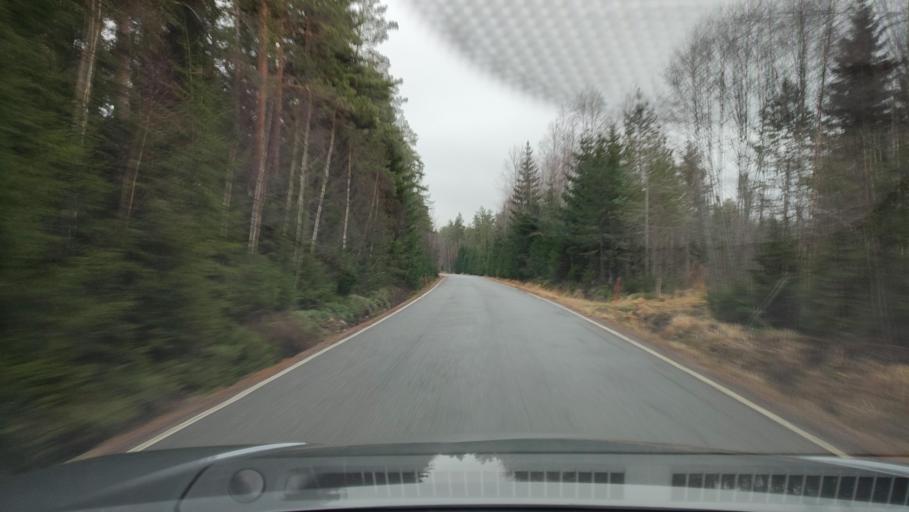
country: FI
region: Southern Ostrobothnia
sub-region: Suupohja
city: Isojoki
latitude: 62.1652
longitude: 21.8912
